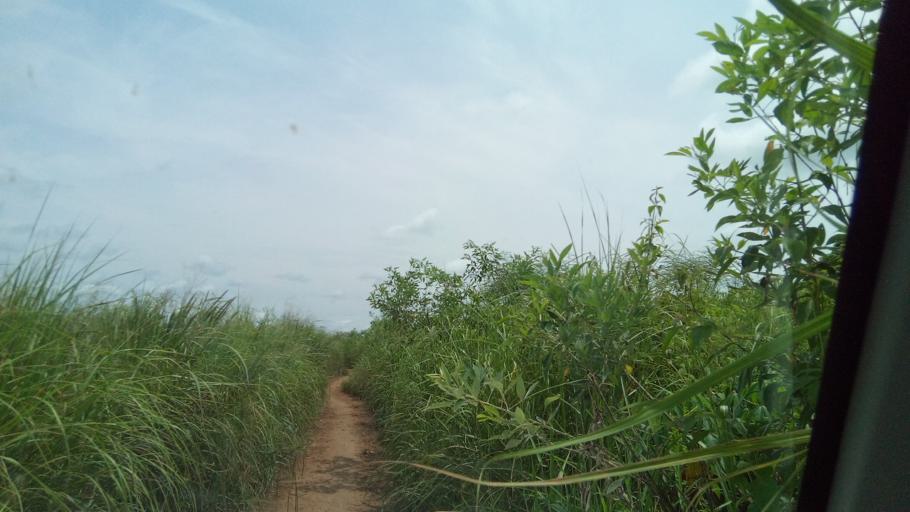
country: AO
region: Zaire
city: Mbanza Congo
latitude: -5.7968
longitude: 13.9953
